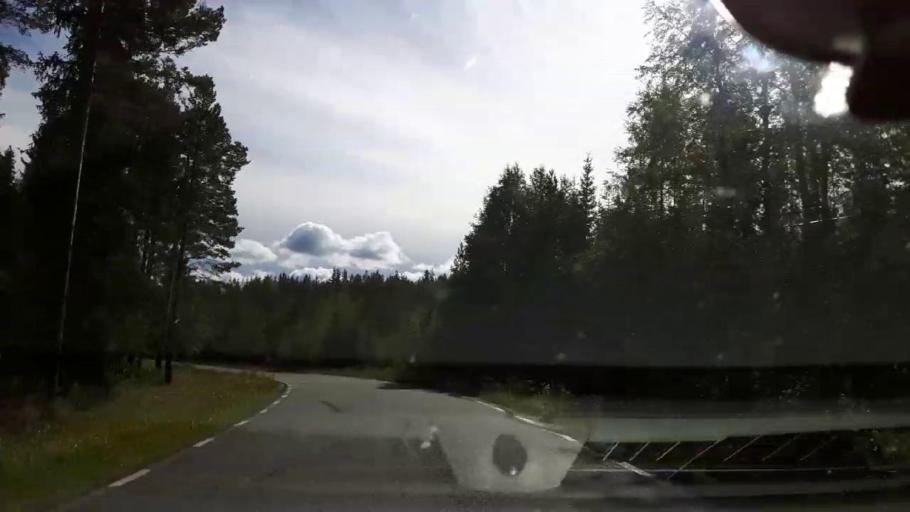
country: SE
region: Jaemtland
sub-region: Braecke Kommun
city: Braecke
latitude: 63.2049
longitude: 15.3545
